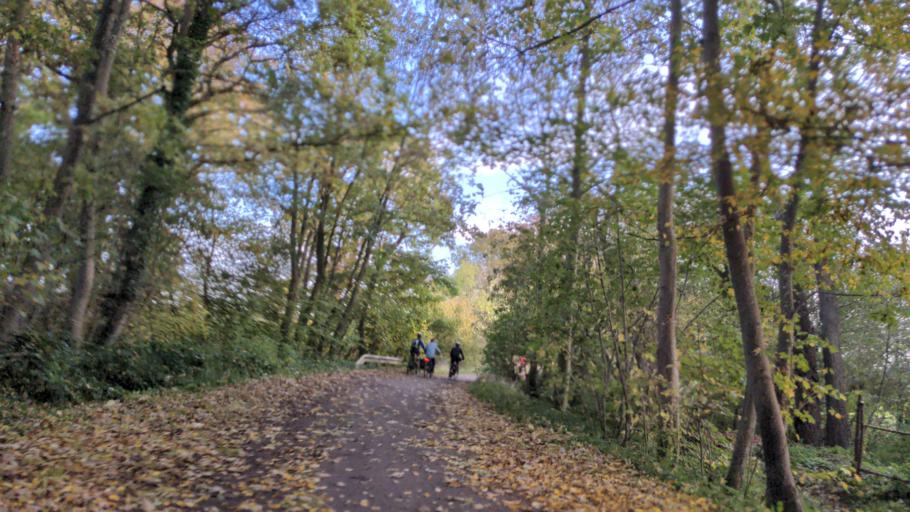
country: DE
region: Schleswig-Holstein
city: Neustadt in Holstein
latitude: 54.1303
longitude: 10.7817
